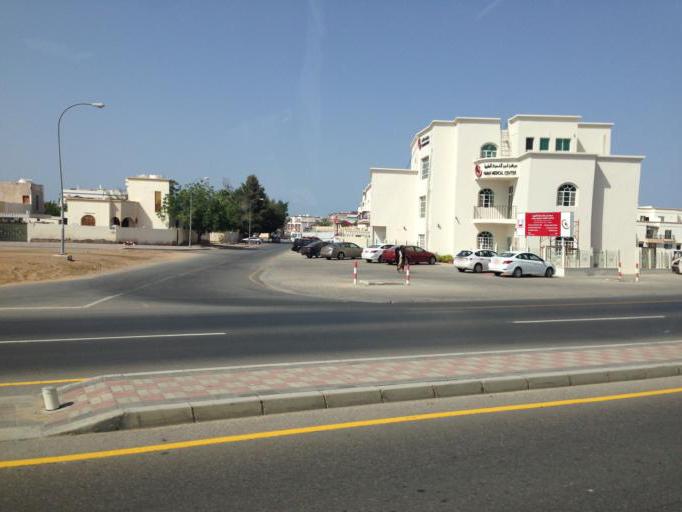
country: OM
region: Muhafazat Masqat
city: Bawshar
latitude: 23.5993
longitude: 58.3815
